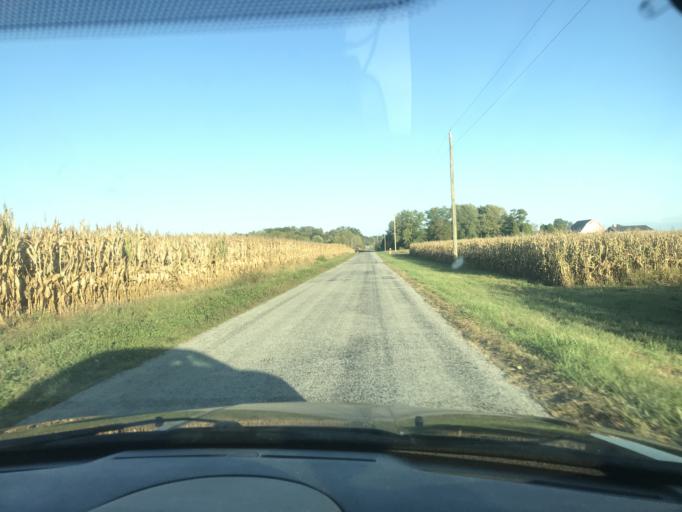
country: US
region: Ohio
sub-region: Logan County
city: West Liberty
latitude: 40.2316
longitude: -83.8041
